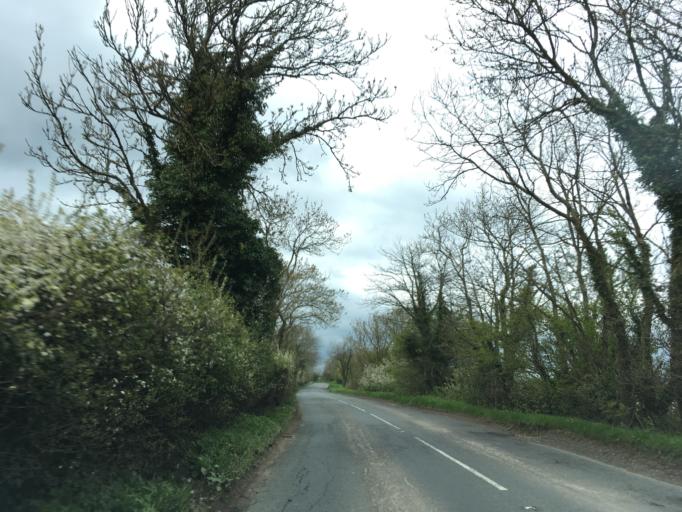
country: GB
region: England
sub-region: Gloucestershire
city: Stonehouse
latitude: 51.6952
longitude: -2.2839
